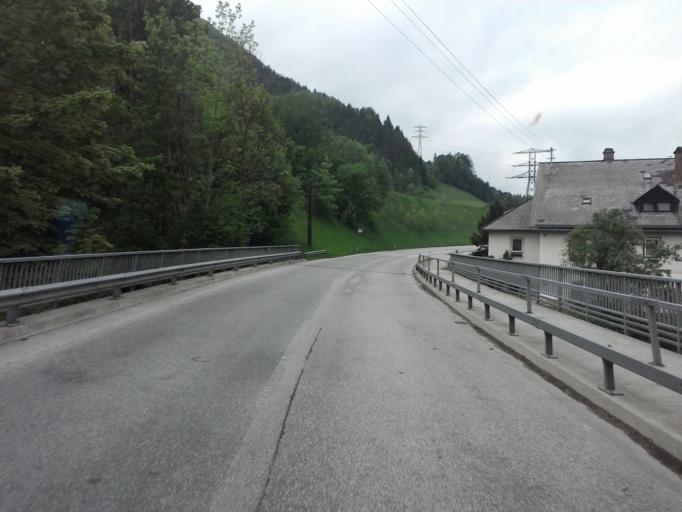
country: AT
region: Styria
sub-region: Politischer Bezirk Liezen
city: Landl
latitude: 47.6491
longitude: 14.7490
